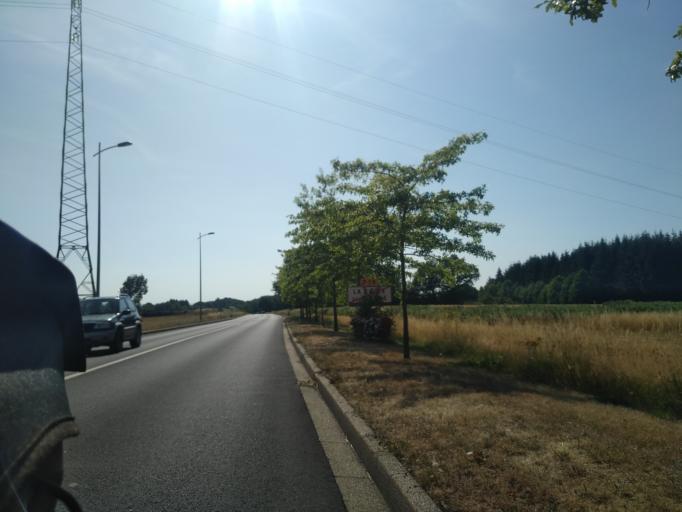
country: FR
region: Auvergne
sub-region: Departement du Puy-de-Dome
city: Saint-Georges-de-Mons
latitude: 45.9435
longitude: 2.8463
